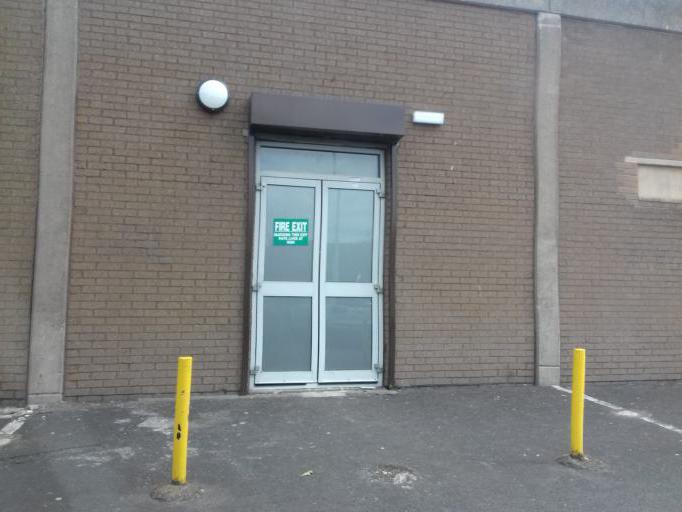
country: IE
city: Greenhills
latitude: 53.3306
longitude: -6.3021
